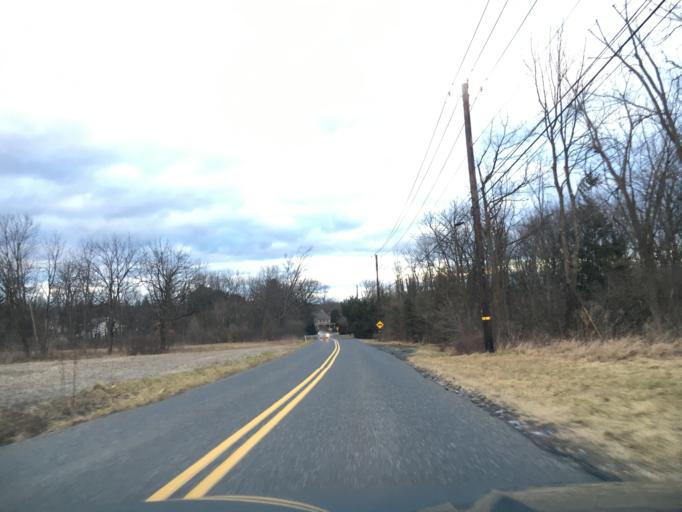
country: US
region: Pennsylvania
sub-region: Lehigh County
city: Schnecksville
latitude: 40.6915
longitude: -75.6079
